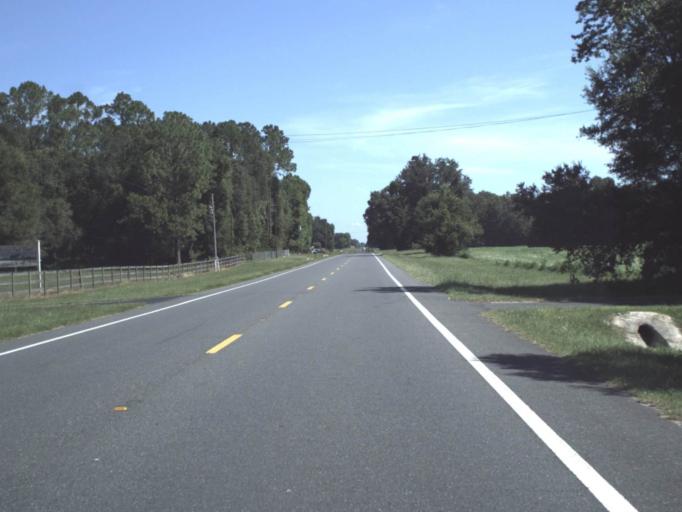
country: US
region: Florida
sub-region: Levy County
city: Williston
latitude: 29.3400
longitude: -82.4558
